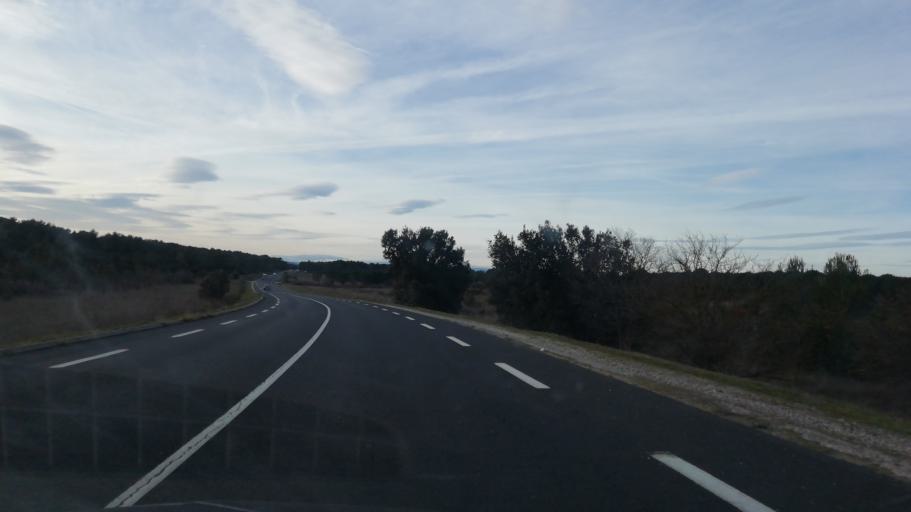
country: FR
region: Languedoc-Roussillon
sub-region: Departement du Gard
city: Caveirac
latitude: 43.8526
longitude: 4.2714
